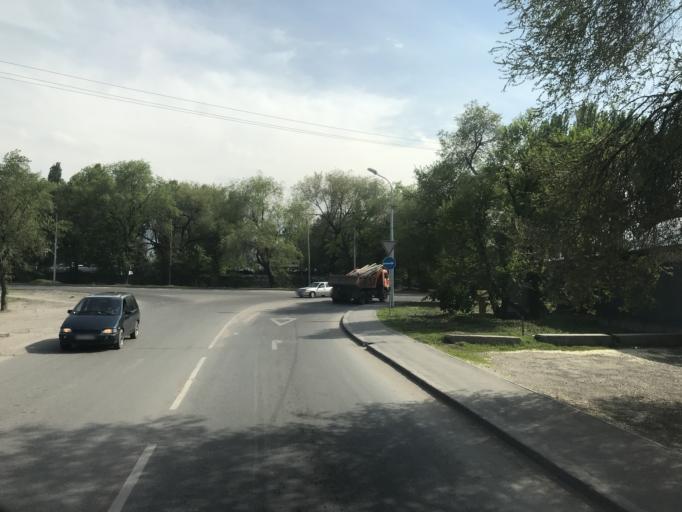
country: KZ
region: Almaty Qalasy
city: Almaty
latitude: 43.2402
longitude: 76.8059
